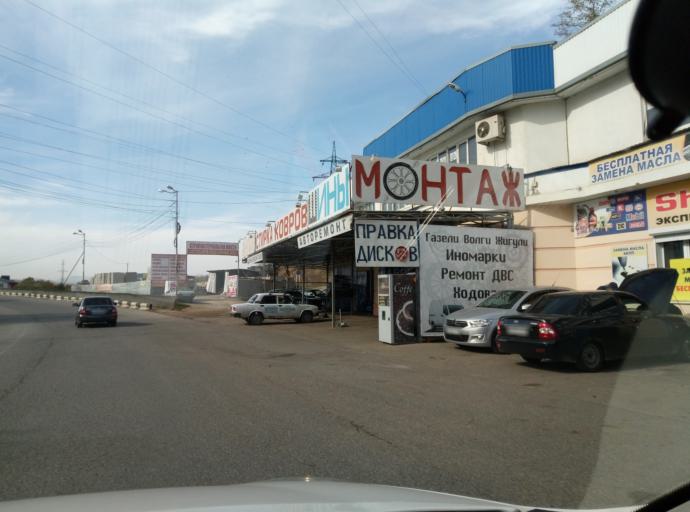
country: RU
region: Stavropol'skiy
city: Kislovodsk
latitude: 43.9325
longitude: 42.7196
